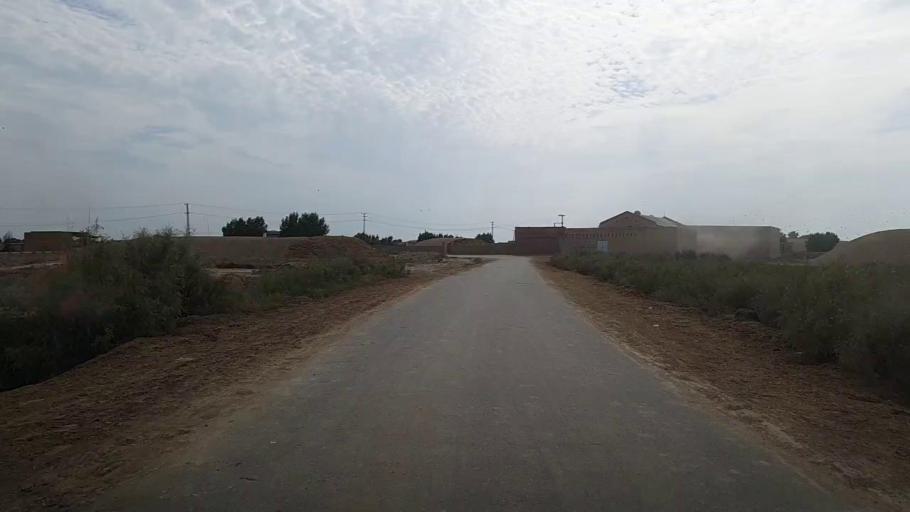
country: PK
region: Sindh
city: Thul
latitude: 28.2583
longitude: 68.7757
